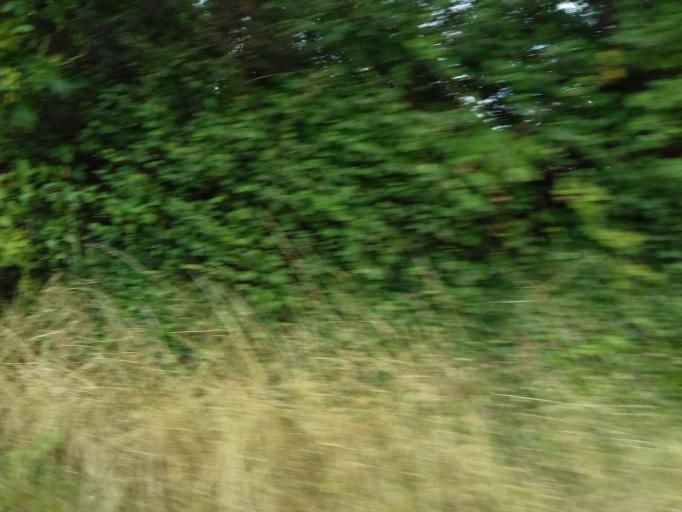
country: IE
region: Leinster
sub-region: Loch Garman
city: Ballinroad
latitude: 52.4839
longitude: -6.4338
